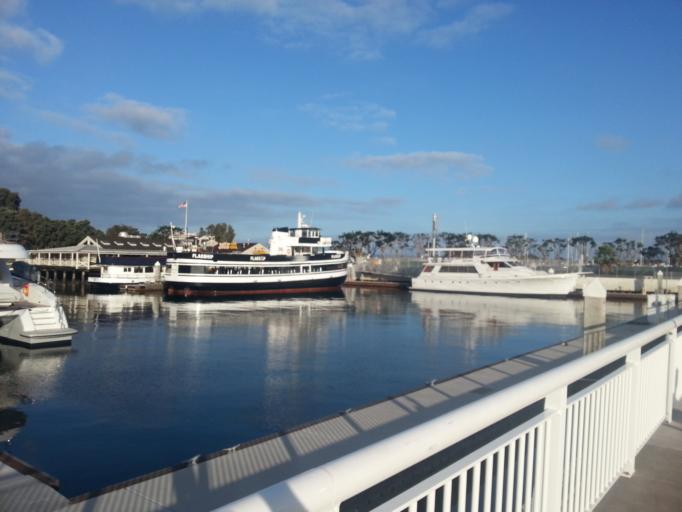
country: US
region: California
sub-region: San Diego County
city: San Diego
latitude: 32.7049
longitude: -117.1622
